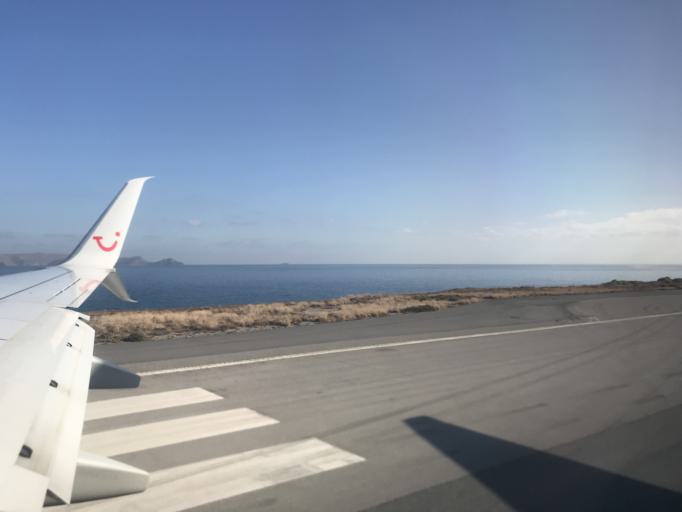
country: GR
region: Crete
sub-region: Nomos Irakleiou
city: Nea Alikarnassos
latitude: 35.3392
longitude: 25.1893
